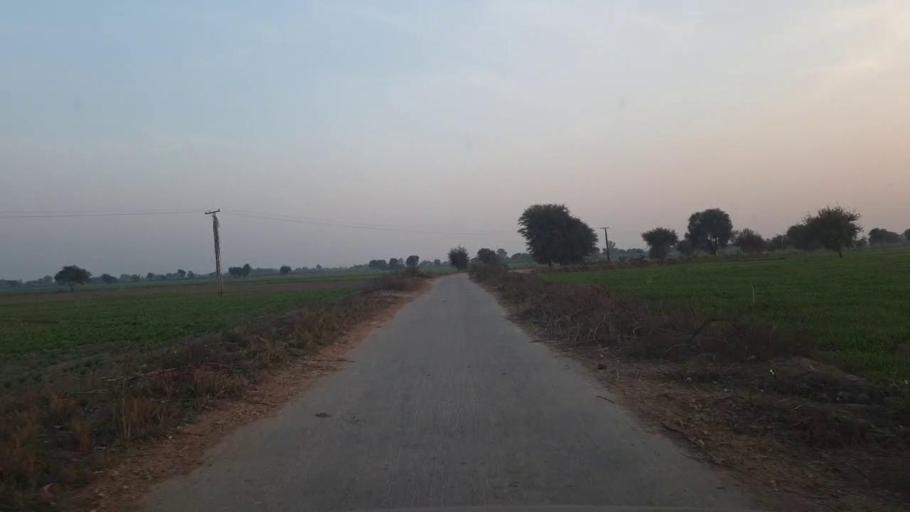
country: PK
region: Sindh
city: Bhit Shah
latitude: 25.8571
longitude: 68.5141
